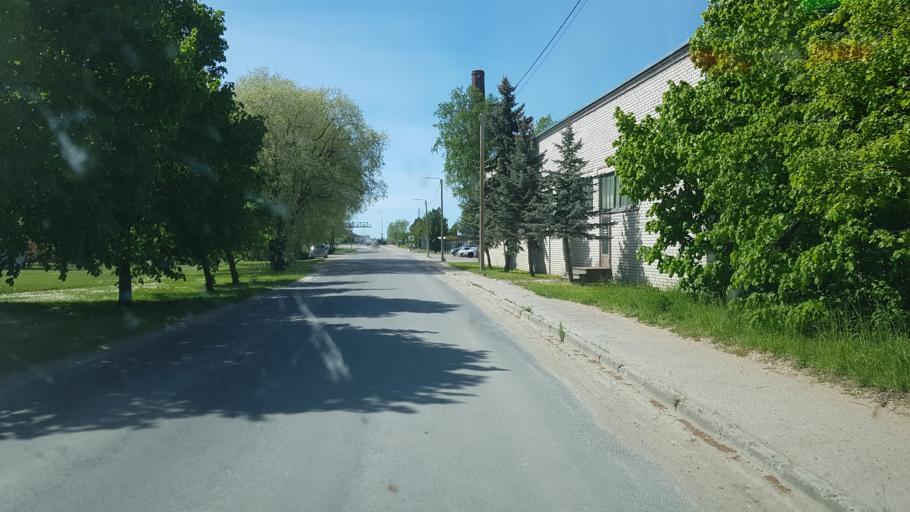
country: EE
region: Saare
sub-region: Kuressaare linn
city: Kuressaare
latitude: 58.2703
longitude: 22.4923
